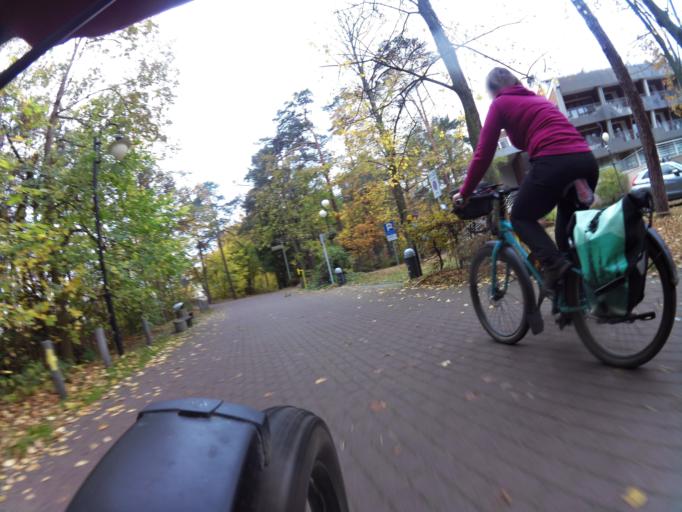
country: PL
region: Pomeranian Voivodeship
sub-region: Powiat pucki
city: Jastarnia
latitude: 54.6994
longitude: 18.6829
